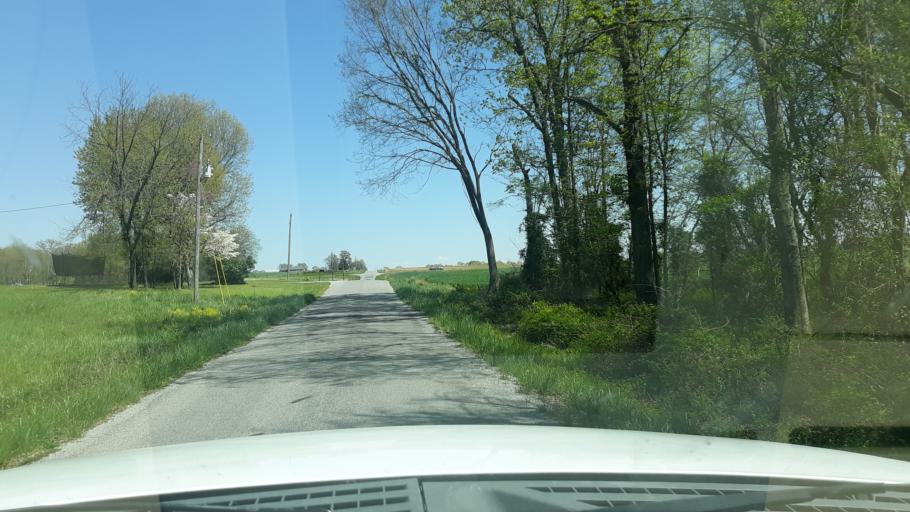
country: US
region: Illinois
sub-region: Saline County
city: Harrisburg
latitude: 37.8849
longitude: -88.6548
